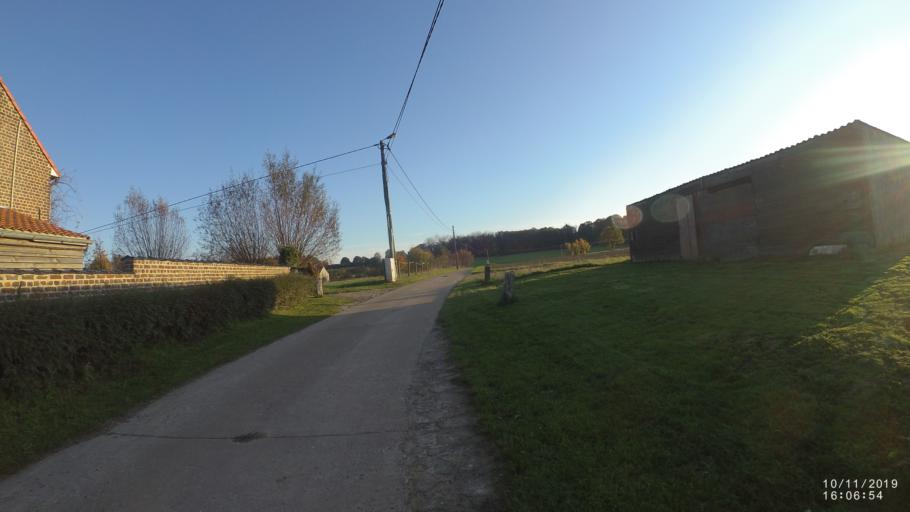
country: BE
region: Flanders
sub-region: Provincie Vlaams-Brabant
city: Lubbeek
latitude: 50.8988
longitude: 4.8555
